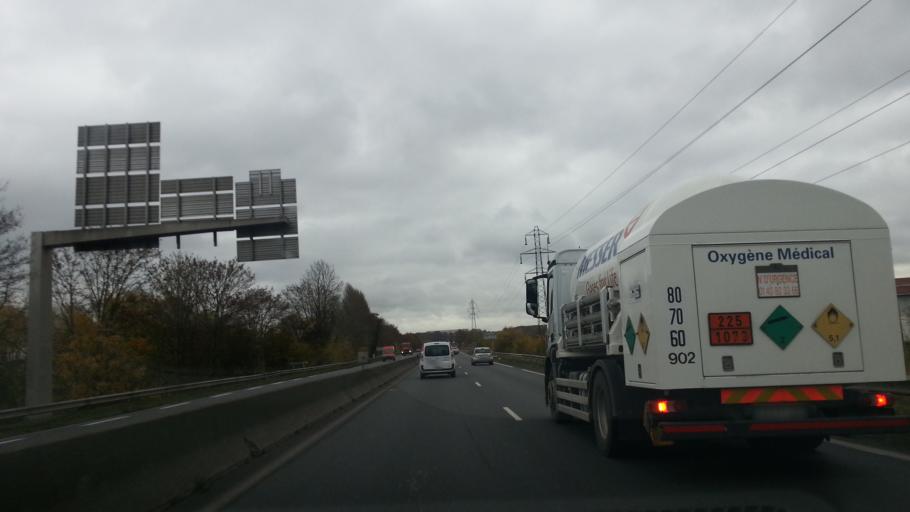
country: FR
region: Picardie
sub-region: Departement de l'Oise
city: Villers-Saint-Paul
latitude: 49.2813
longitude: 2.4793
